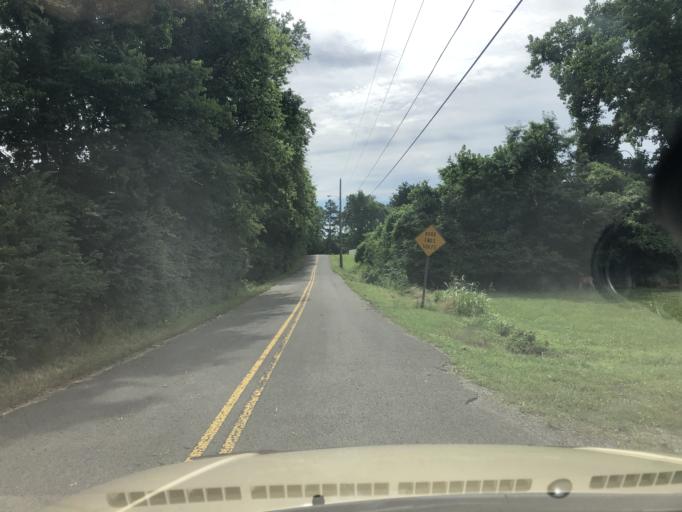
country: US
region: Tennessee
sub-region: Davidson County
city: Lakewood
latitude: 36.2169
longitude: -86.6454
